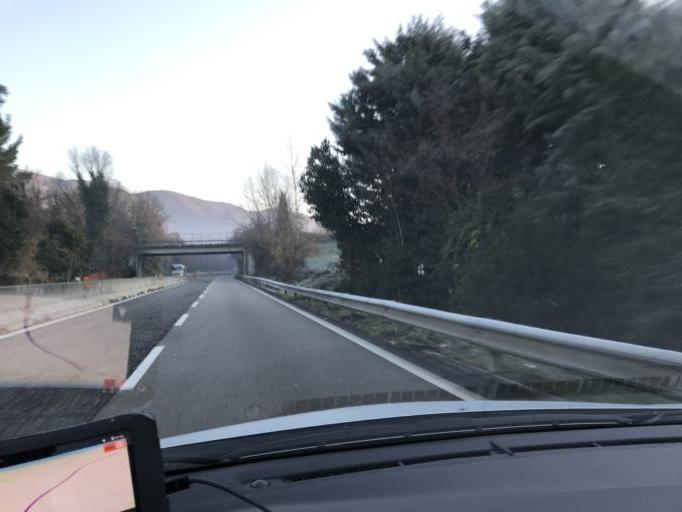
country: IT
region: Umbria
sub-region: Provincia di Terni
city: Terni
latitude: 42.5802
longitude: 12.6373
